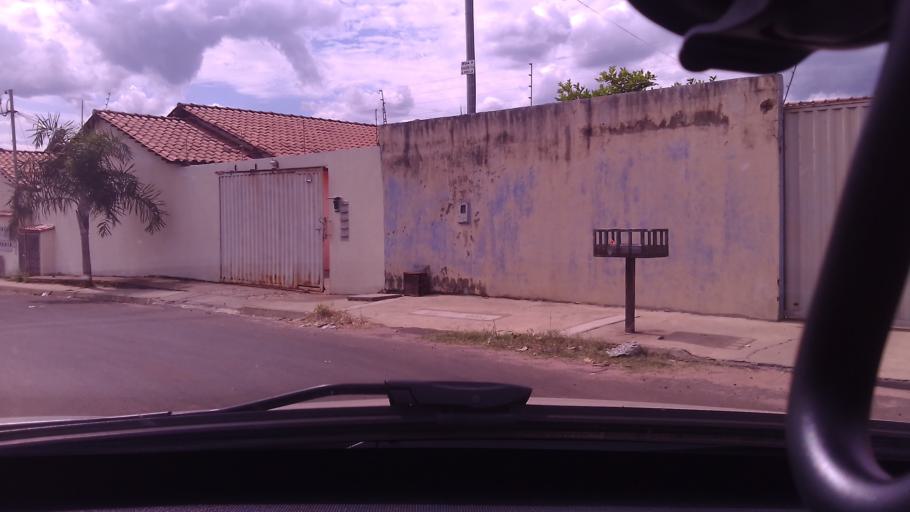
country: BR
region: Goias
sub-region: Mineiros
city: Mineiros
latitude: -17.5812
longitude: -52.5457
